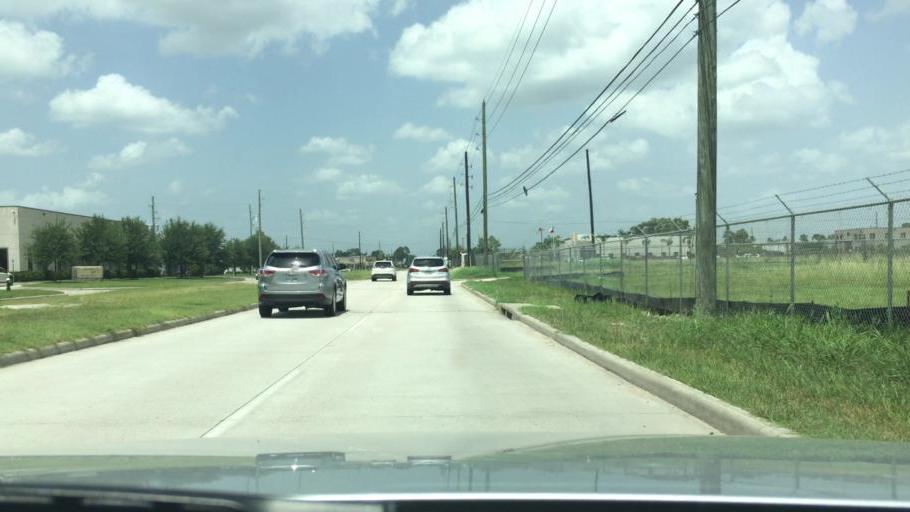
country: US
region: Texas
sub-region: Harris County
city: Hudson
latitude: 29.9569
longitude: -95.5252
